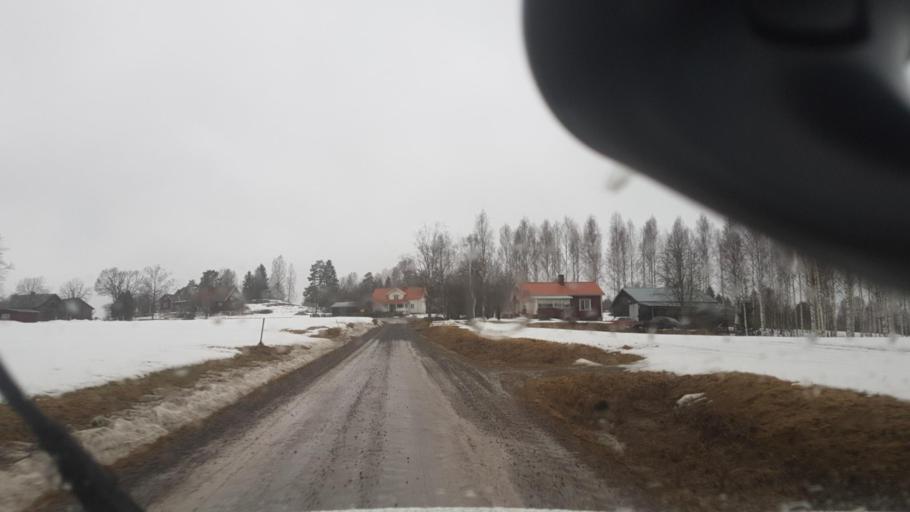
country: SE
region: Vaermland
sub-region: Eda Kommun
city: Charlottenberg
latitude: 59.8480
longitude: 12.3471
